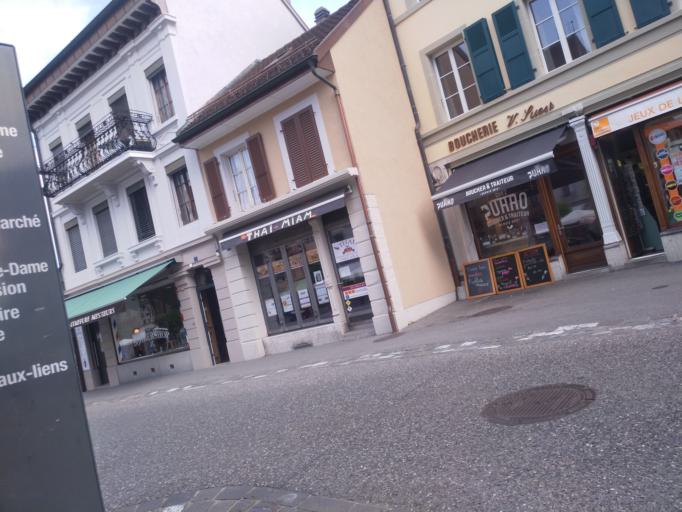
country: CH
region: Fribourg
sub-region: Gruyere District
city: Bulle
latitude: 46.6175
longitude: 7.0572
